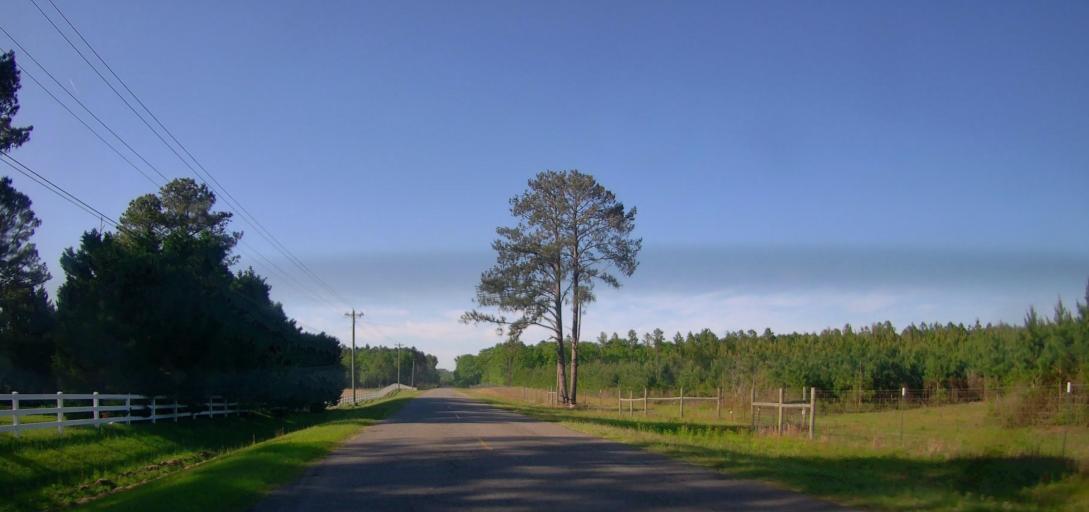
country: US
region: Georgia
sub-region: Houston County
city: Perry
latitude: 32.4526
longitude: -83.8172
